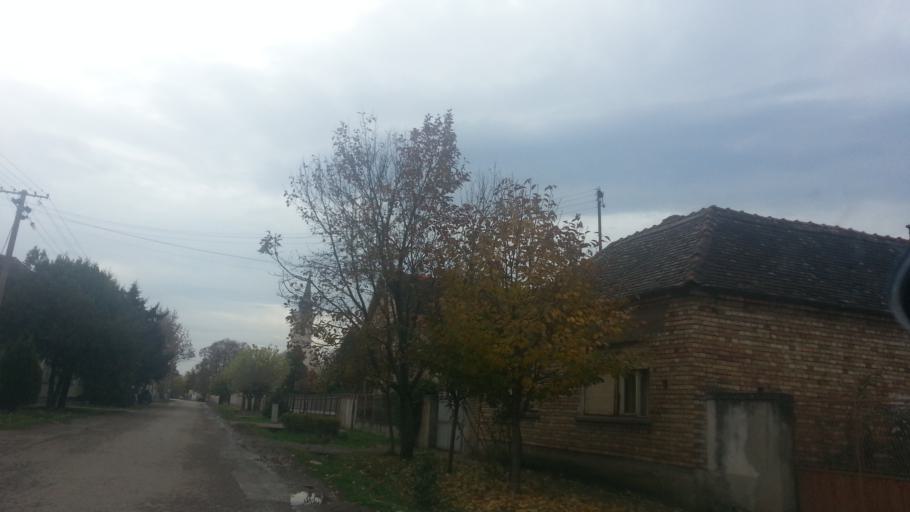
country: RS
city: Golubinci
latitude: 44.9874
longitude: 20.0654
